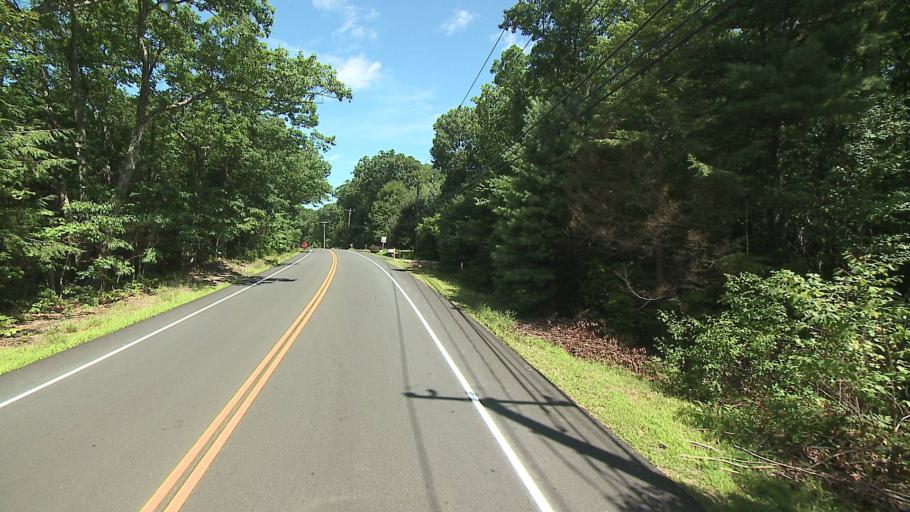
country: US
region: Connecticut
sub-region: Litchfield County
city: New Hartford Center
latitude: 41.9534
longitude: -72.9151
